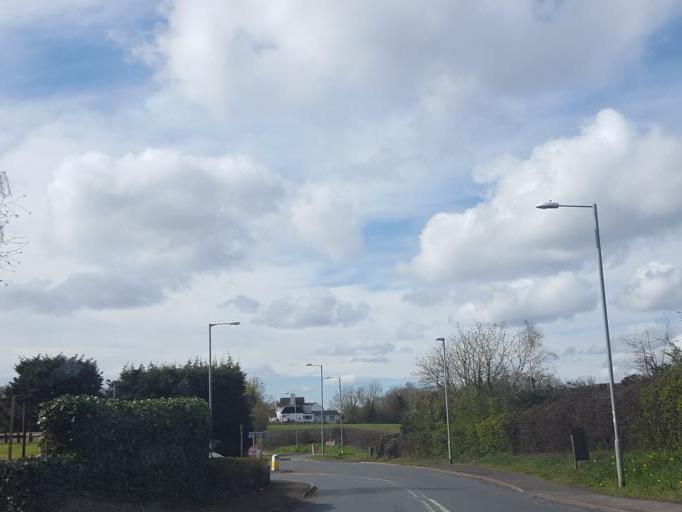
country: GB
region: England
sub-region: Worcestershire
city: Bransford
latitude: 52.1717
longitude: -2.2984
